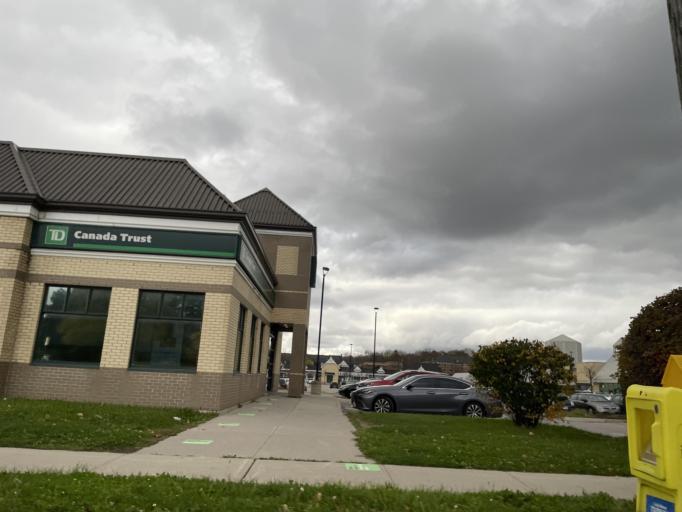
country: CA
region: Ontario
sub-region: Wellington County
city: Guelph
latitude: 43.5203
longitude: -80.2335
